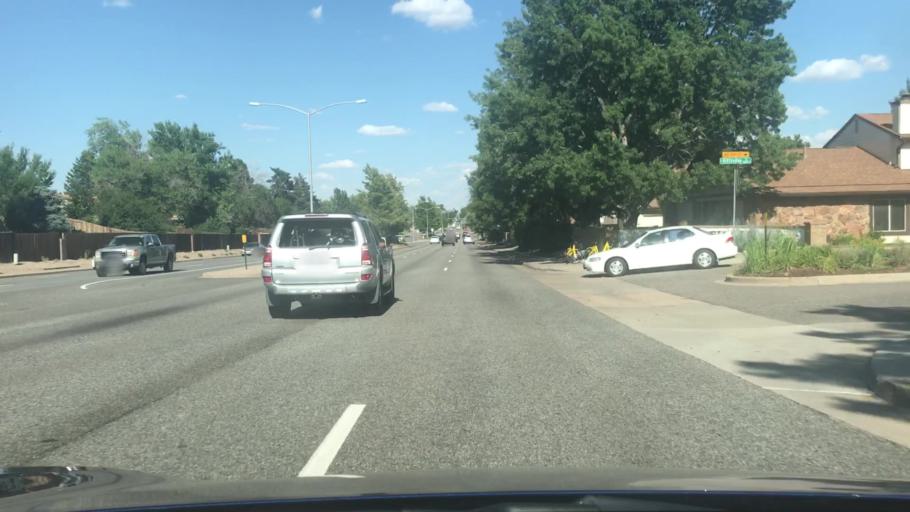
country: US
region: Colorado
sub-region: Arapahoe County
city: Dove Valley
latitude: 39.6530
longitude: -104.8019
